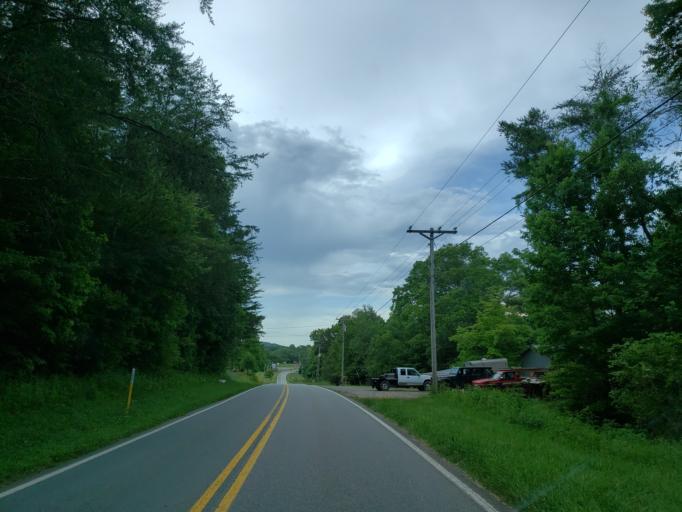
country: US
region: Georgia
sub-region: Fannin County
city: Blue Ridge
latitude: 34.8662
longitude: -84.3692
